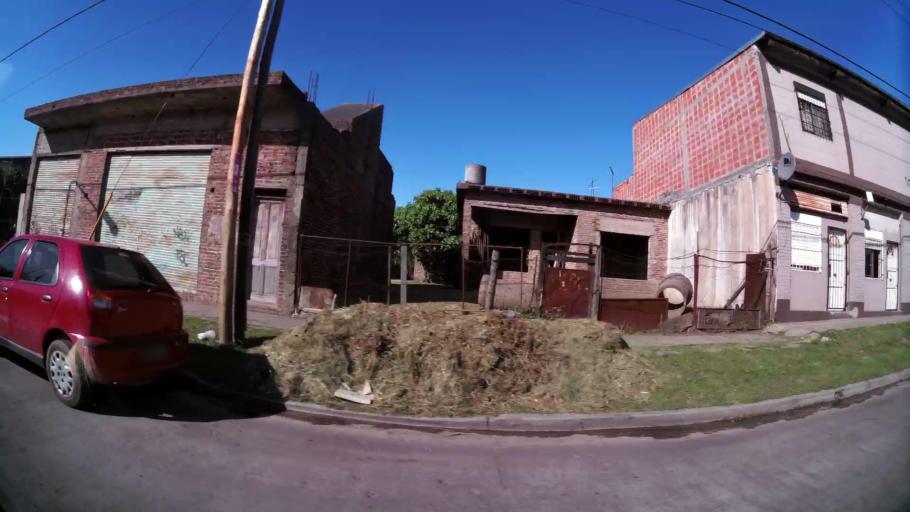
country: AR
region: Buenos Aires
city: Santa Catalina - Dique Lujan
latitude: -34.4815
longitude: -58.6700
